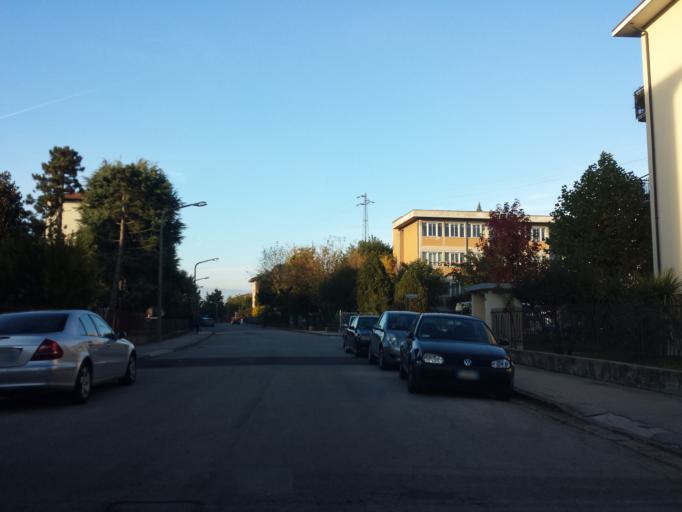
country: IT
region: Veneto
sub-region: Provincia di Vicenza
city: Vicenza
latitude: 45.5741
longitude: 11.5430
